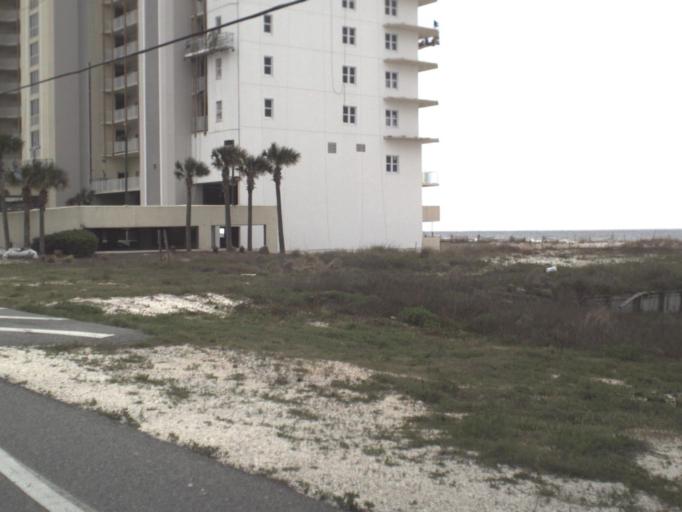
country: US
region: Alabama
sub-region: Baldwin County
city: Orange Beach
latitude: 30.2948
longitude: -87.4461
